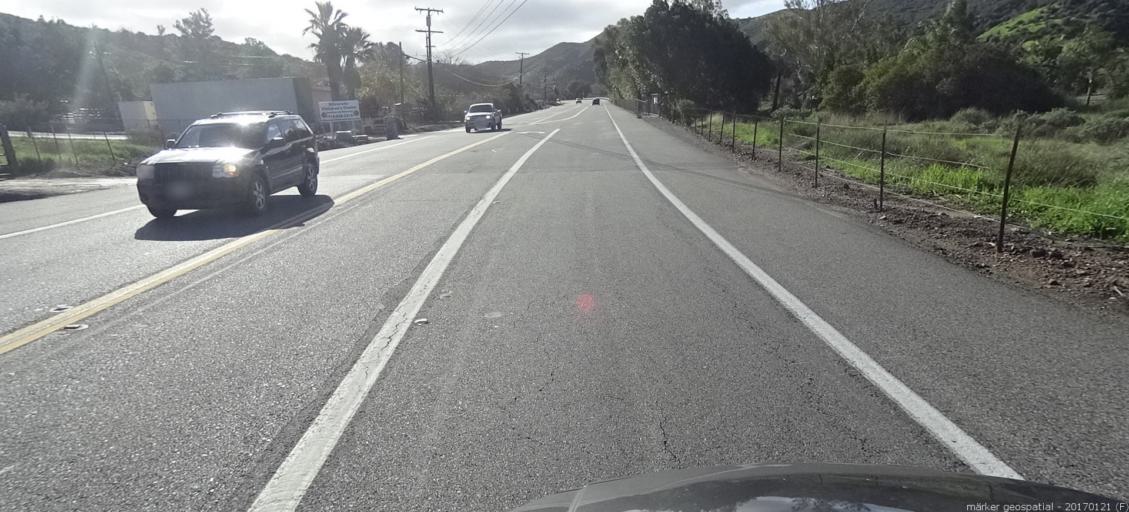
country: US
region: California
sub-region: Orange County
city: Foothill Ranch
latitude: 33.7460
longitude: -117.6688
